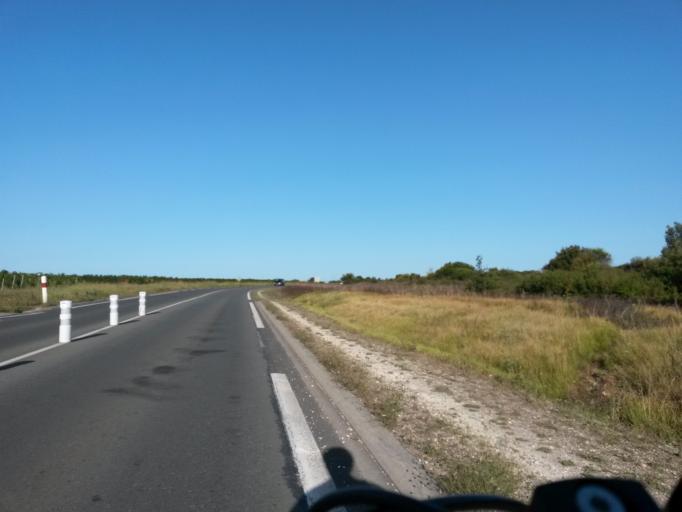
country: FR
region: Poitou-Charentes
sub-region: Departement de la Charente-Maritime
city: Rivedoux-Plage
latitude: 46.1528
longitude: -1.2829
